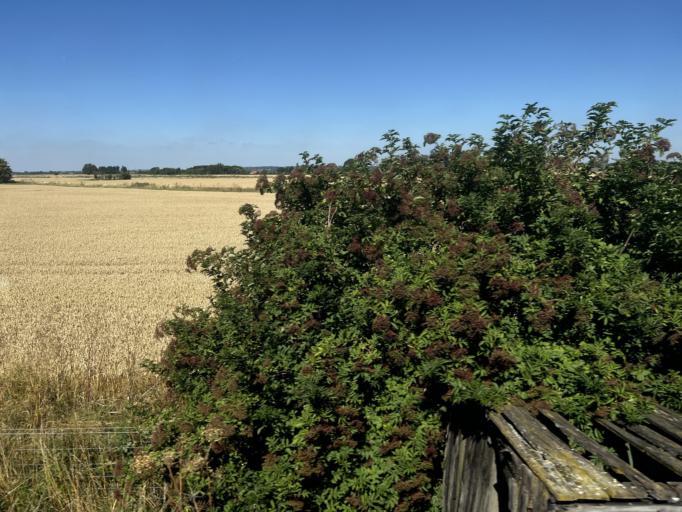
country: GB
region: England
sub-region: Lincolnshire
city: Spilsby
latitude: 53.1209
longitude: 0.1371
